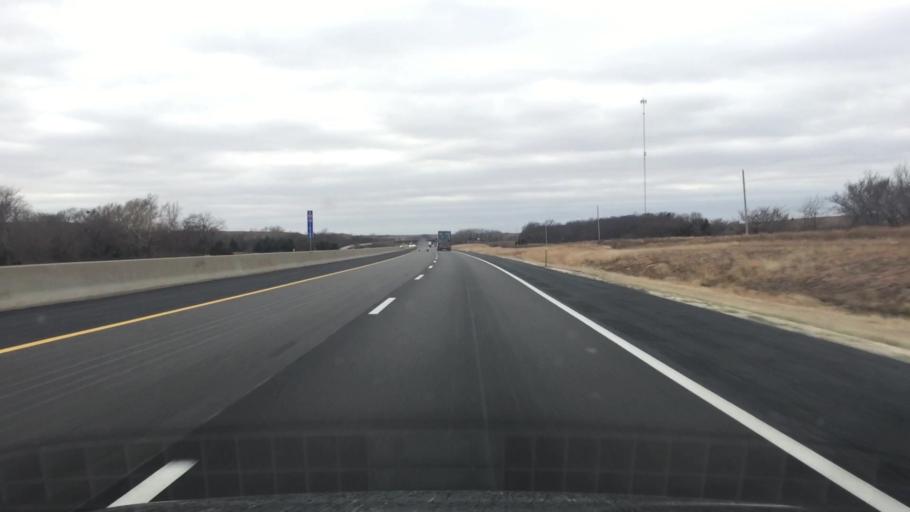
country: US
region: Kansas
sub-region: Chase County
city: Cottonwood Falls
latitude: 38.1480
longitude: -96.5038
